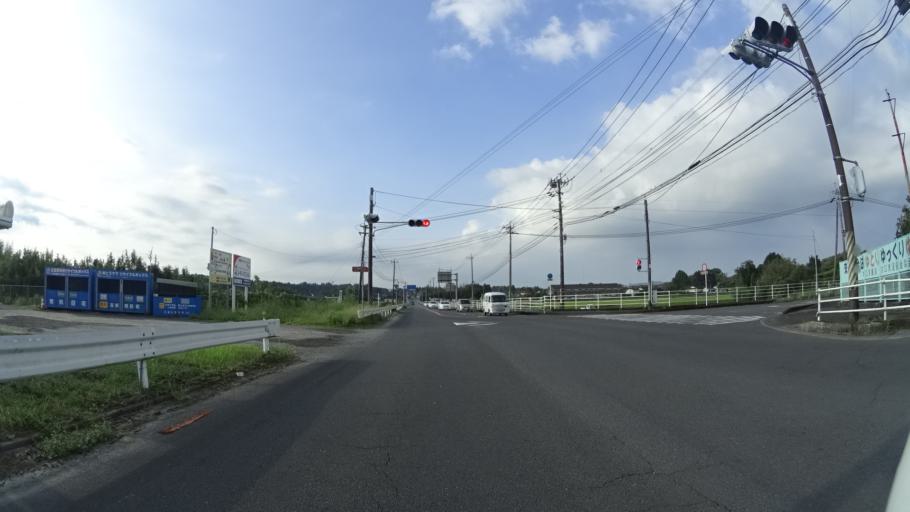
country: JP
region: Kagoshima
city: Okuchi-shinohara
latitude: 32.0499
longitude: 130.5973
